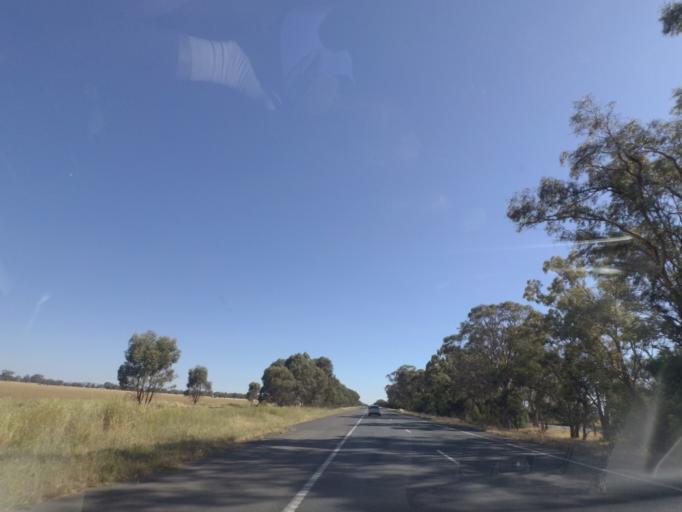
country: AU
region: Victoria
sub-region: Greater Shepparton
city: Shepparton
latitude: -36.7108
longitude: 145.1988
